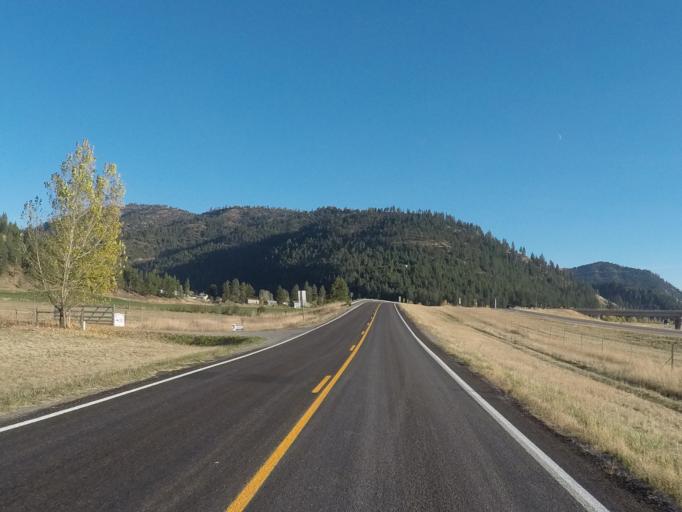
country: US
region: Montana
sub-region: Missoula County
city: Clinton
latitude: 46.7829
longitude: -113.7141
